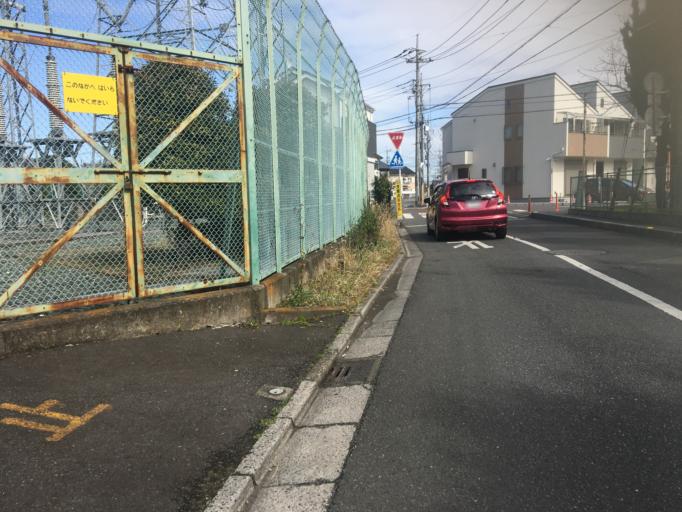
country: JP
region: Saitama
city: Shiki
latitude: 35.8401
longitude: 139.5900
